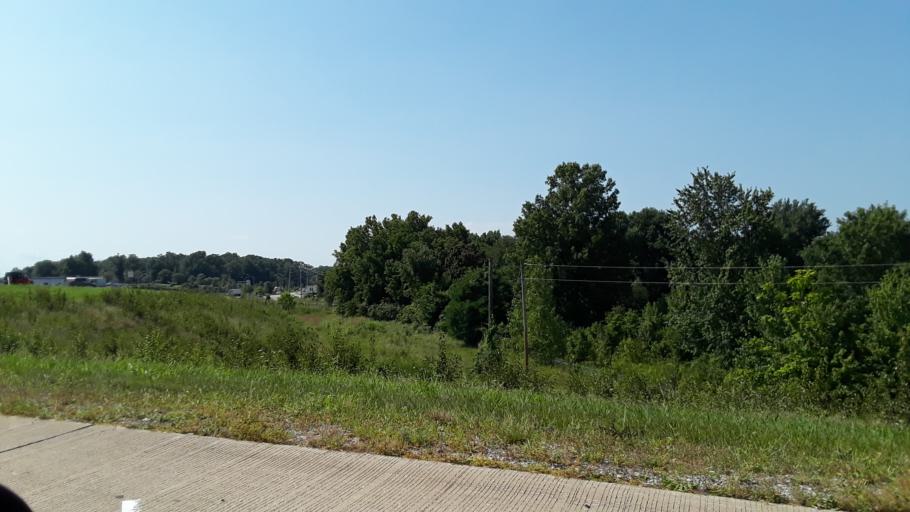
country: US
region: Indiana
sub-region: Clark County
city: Sellersburg
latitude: 38.3705
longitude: -85.7571
